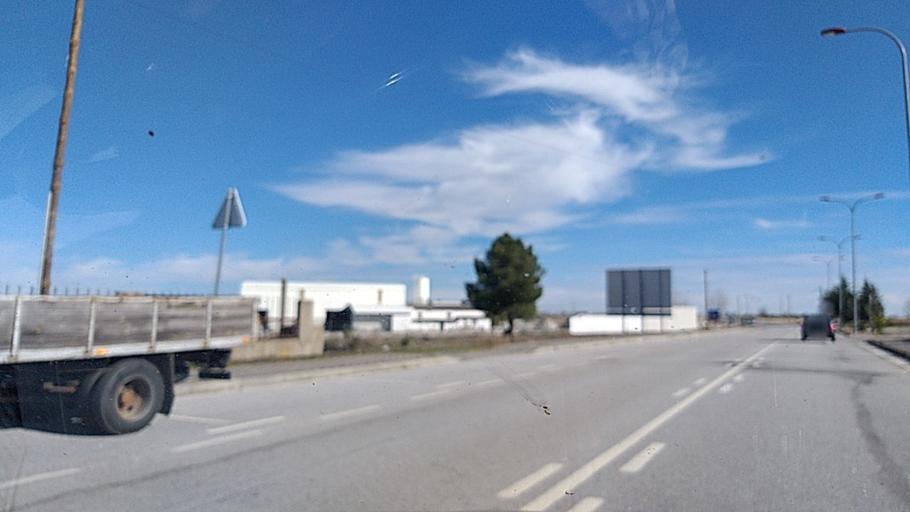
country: ES
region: Castille and Leon
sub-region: Provincia de Salamanca
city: Fuentes de Onoro
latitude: 40.5945
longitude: -6.9919
